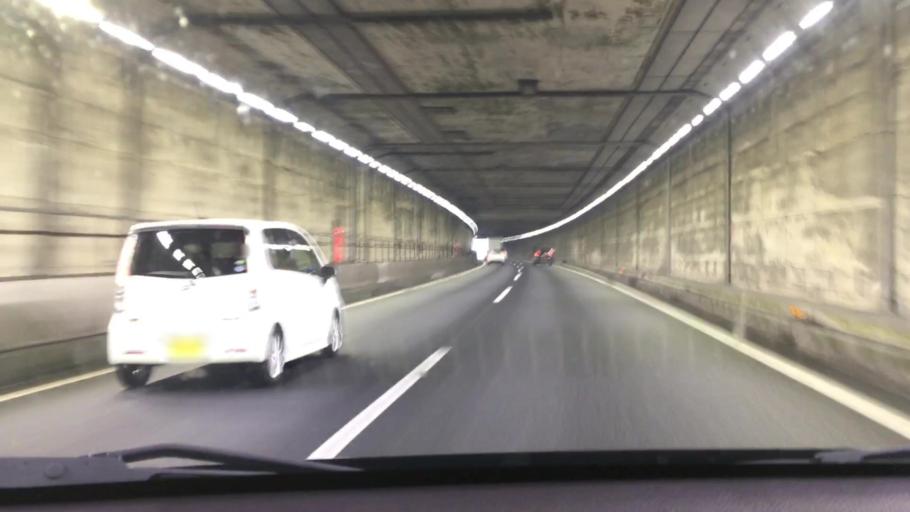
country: JP
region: Kumamoto
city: Uto
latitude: 32.6904
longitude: 130.7378
